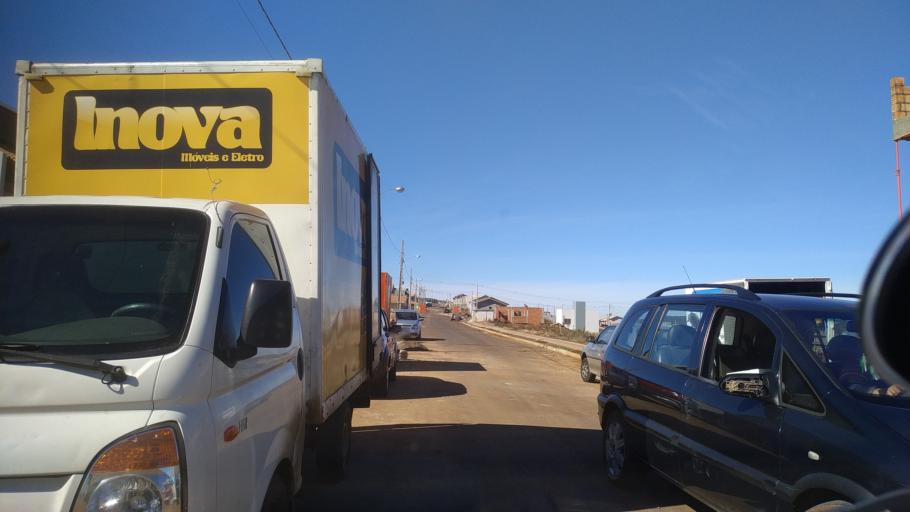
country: BR
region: Santa Catarina
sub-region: Chapeco
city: Chapeco
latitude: -27.0512
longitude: -52.5968
